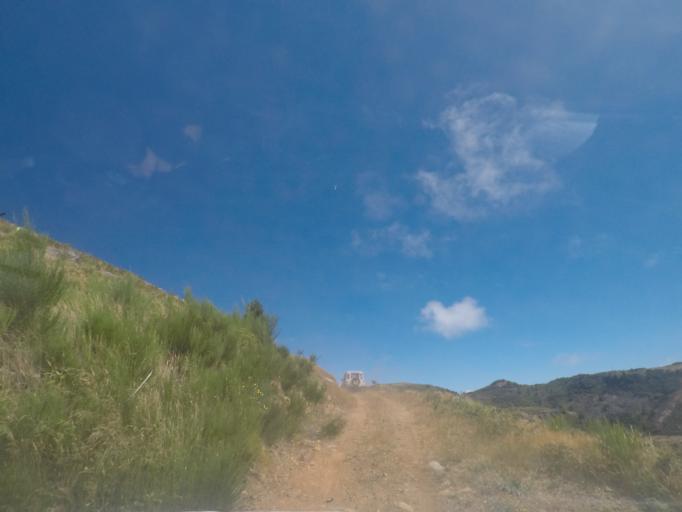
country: PT
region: Madeira
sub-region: Funchal
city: Nossa Senhora do Monte
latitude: 32.7097
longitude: -16.9060
